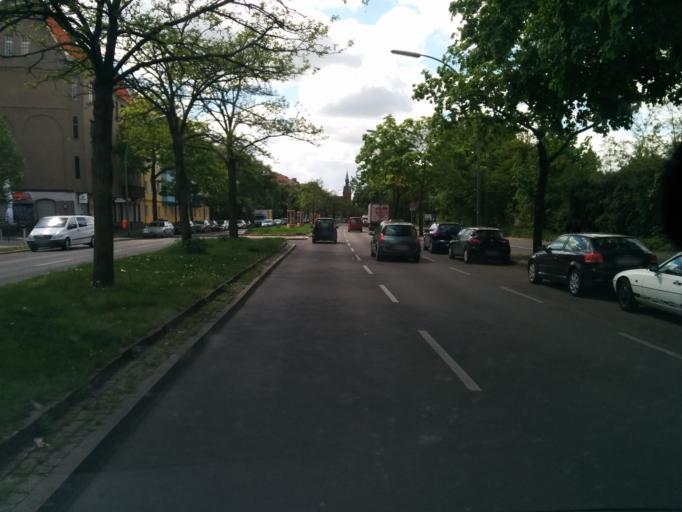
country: DE
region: Berlin
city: Wilhelmstadt
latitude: 52.5246
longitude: 13.1929
